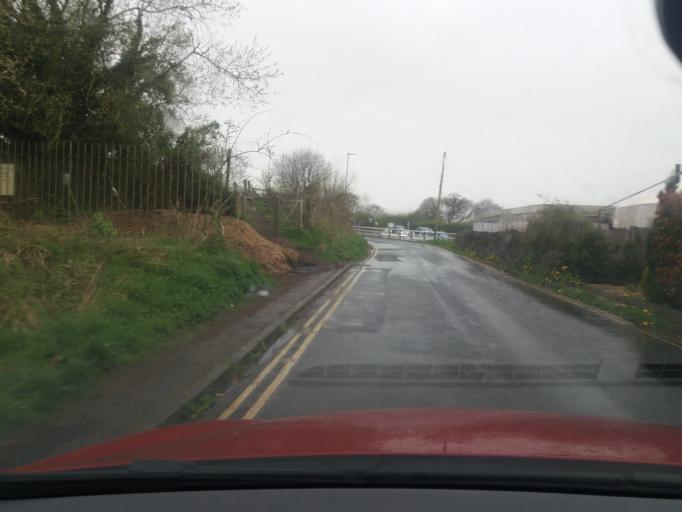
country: GB
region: England
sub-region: Lancashire
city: Chorley
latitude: 53.6874
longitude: -2.6110
